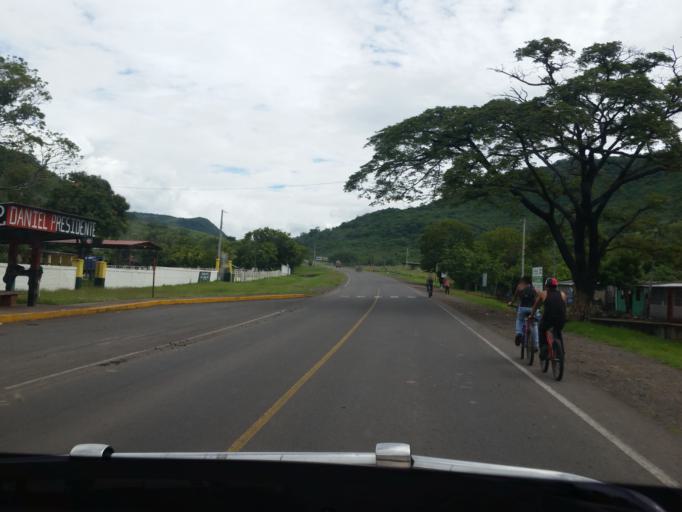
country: NI
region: Matagalpa
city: Matagalpa
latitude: 12.9123
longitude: -86.0213
